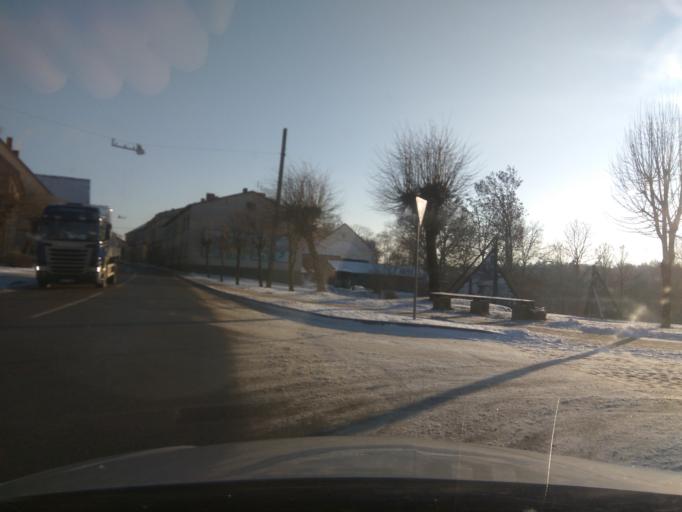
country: LV
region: Aizpute
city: Aizpute
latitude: 56.7207
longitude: 21.6022
